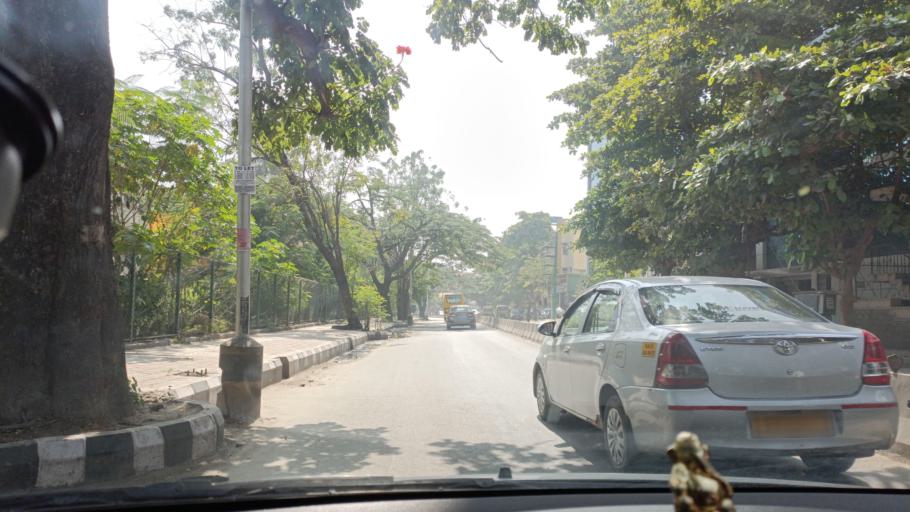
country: IN
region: Karnataka
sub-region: Bangalore Urban
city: Bangalore
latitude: 12.9119
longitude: 77.6149
